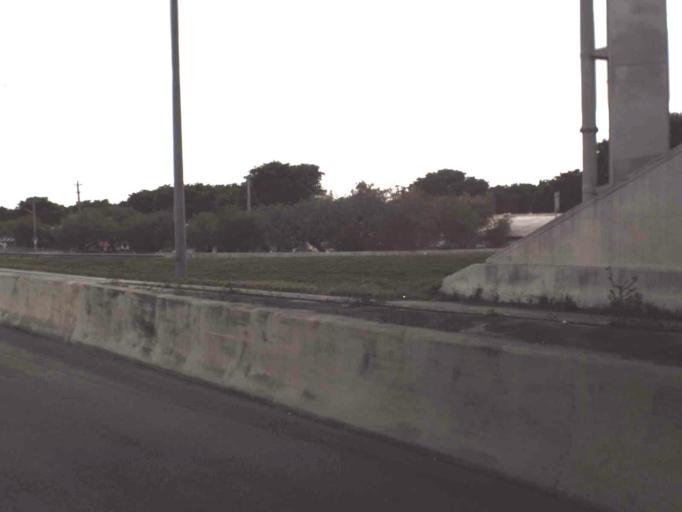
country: US
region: Florida
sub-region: Miami-Dade County
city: Lake Lucerne
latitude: 25.9722
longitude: -80.2298
